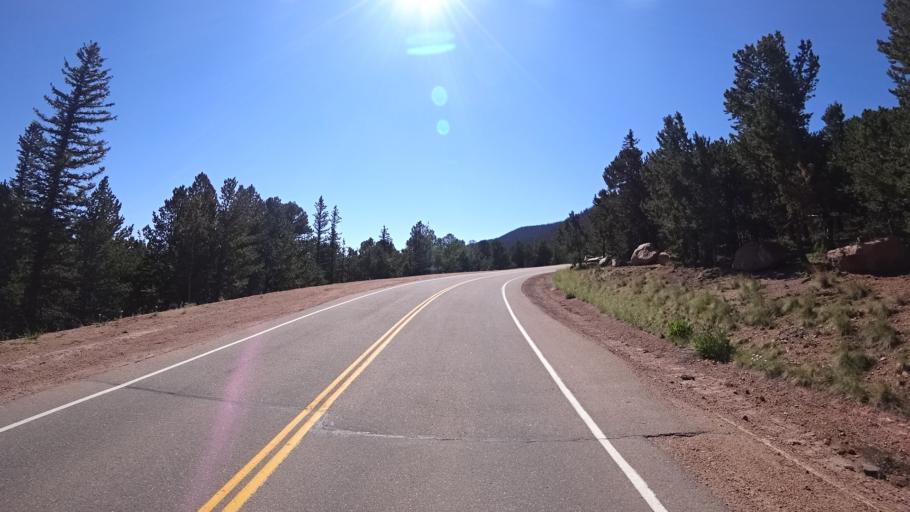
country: US
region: Colorado
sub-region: El Paso County
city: Cascade-Chipita Park
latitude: 38.8984
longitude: -105.0656
